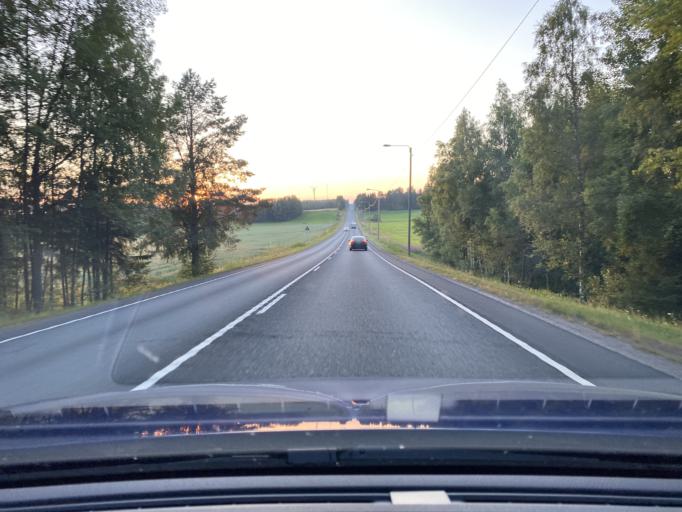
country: FI
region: Pirkanmaa
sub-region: Luoteis-Pirkanmaa
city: Ikaalinen
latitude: 61.7657
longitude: 23.0193
